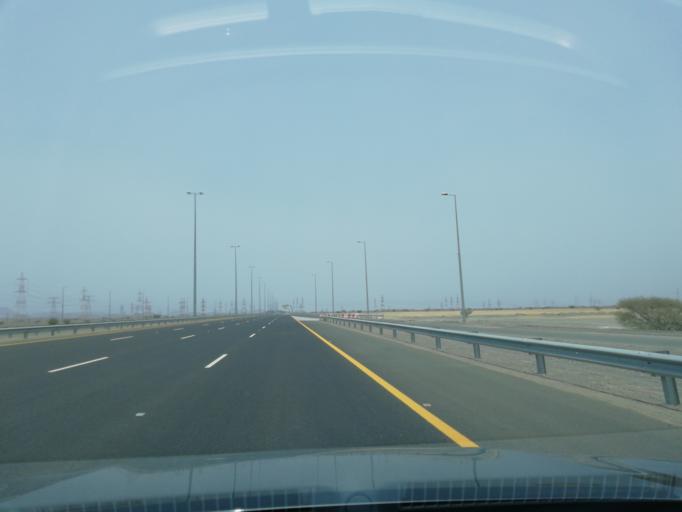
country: OM
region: Al Batinah
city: Al Liwa'
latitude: 24.4083
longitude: 56.5393
